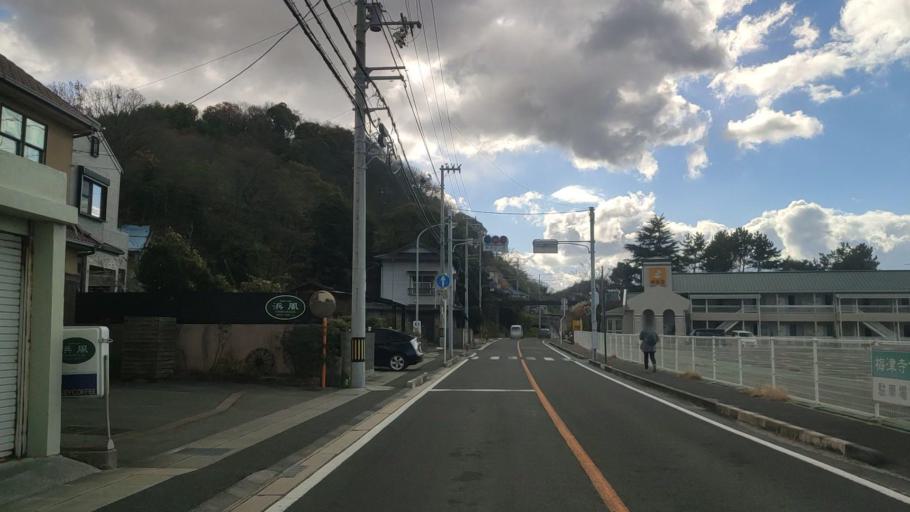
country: JP
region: Ehime
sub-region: Shikoku-chuo Shi
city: Matsuyama
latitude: 33.8744
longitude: 132.7085
